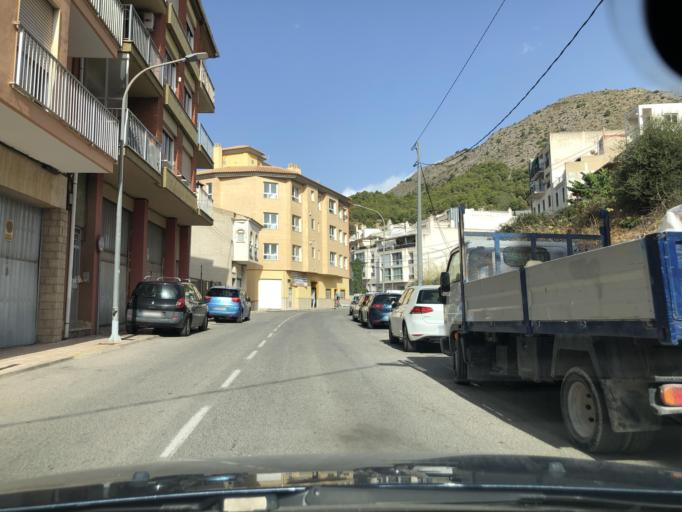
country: ES
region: Valencia
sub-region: Provincia de Alicante
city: Callosa d'En Sarria
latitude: 38.6510
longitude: -0.1260
